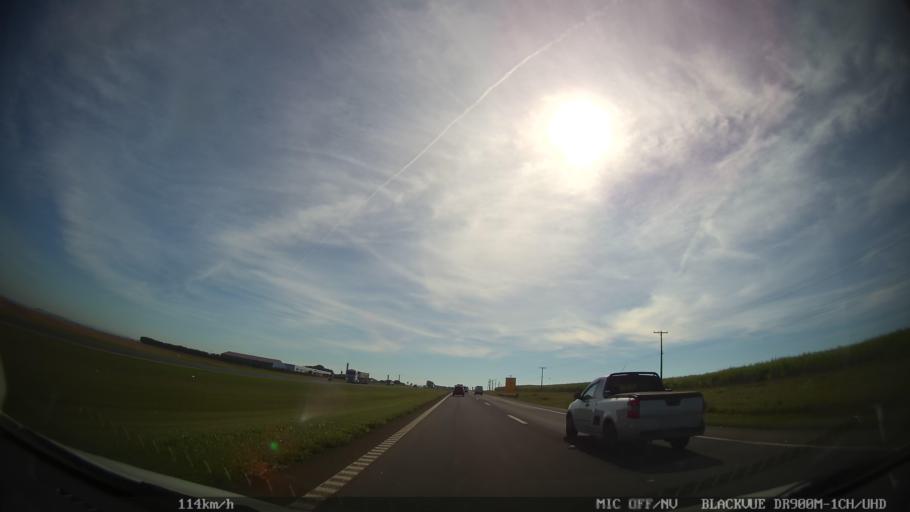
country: BR
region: Sao Paulo
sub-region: Araras
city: Araras
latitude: -22.4223
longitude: -47.3919
